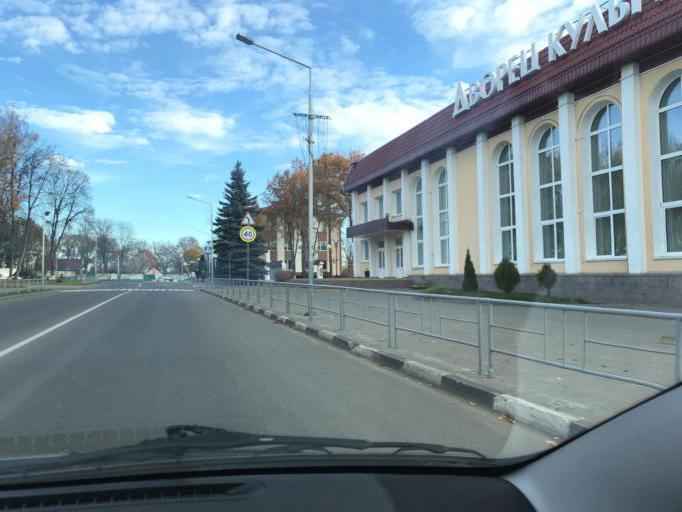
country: BY
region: Vitebsk
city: Haradok
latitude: 55.4608
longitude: 29.9871
